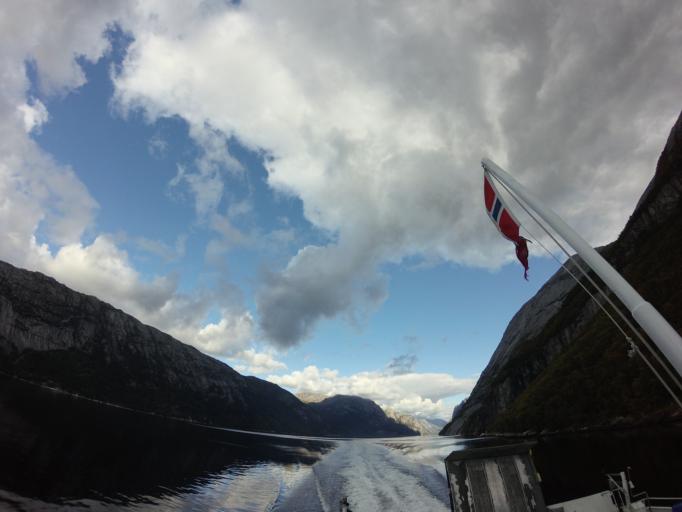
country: NO
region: Rogaland
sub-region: Hjelmeland
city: Hjelmelandsvagen
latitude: 59.0171
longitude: 6.4353
